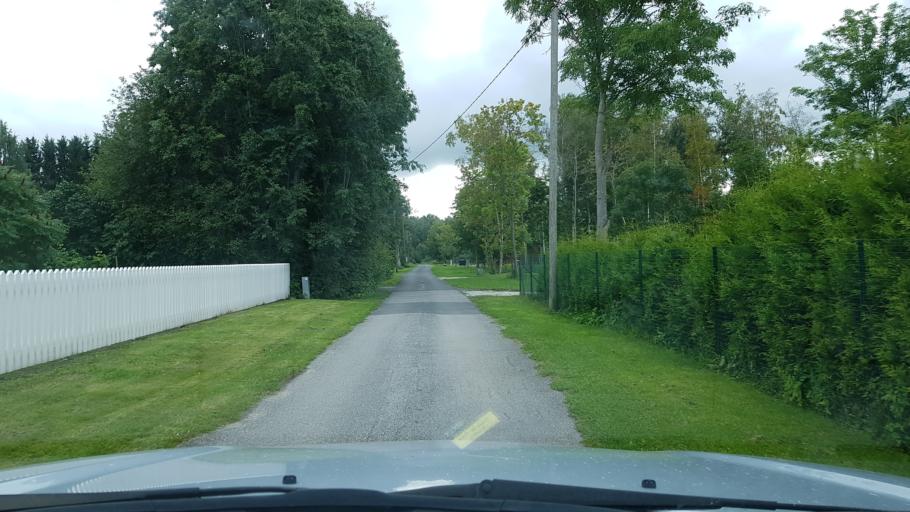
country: EE
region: Harju
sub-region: Rae vald
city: Jueri
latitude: 59.3609
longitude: 24.9397
